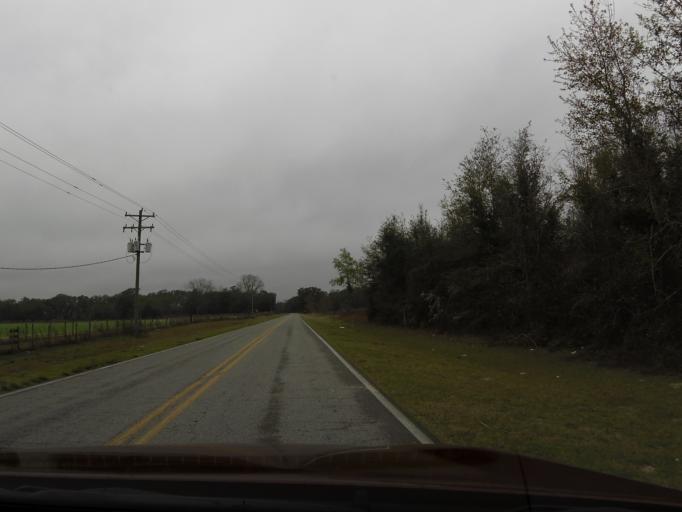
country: US
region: Florida
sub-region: Gilchrist County
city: Trenton
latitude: 29.8026
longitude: -82.9531
